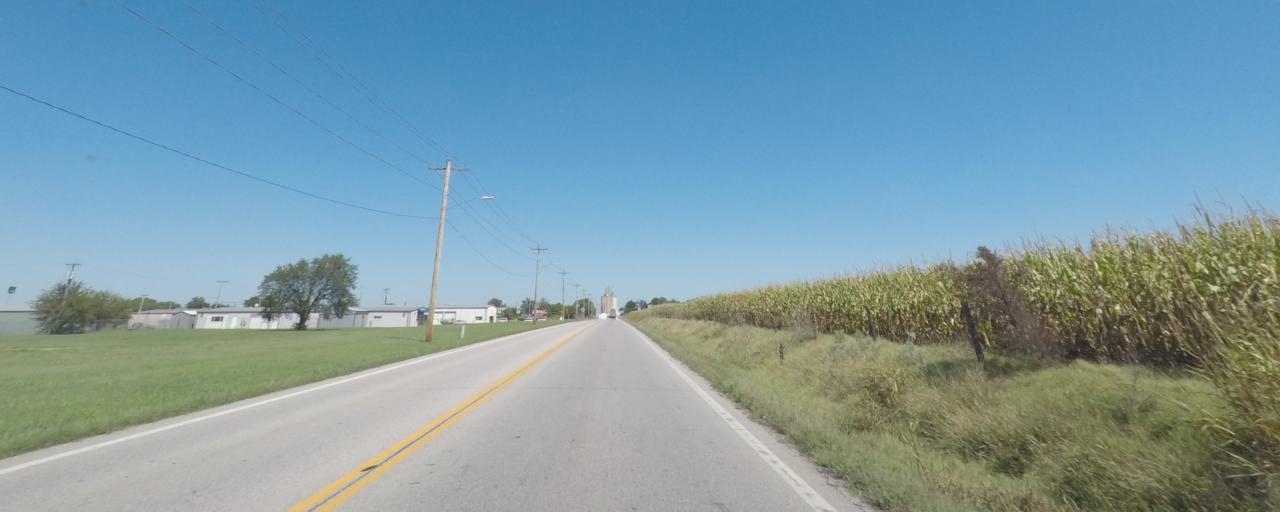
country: US
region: Kansas
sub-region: Sumner County
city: Wellington
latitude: 37.2927
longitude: -97.3943
